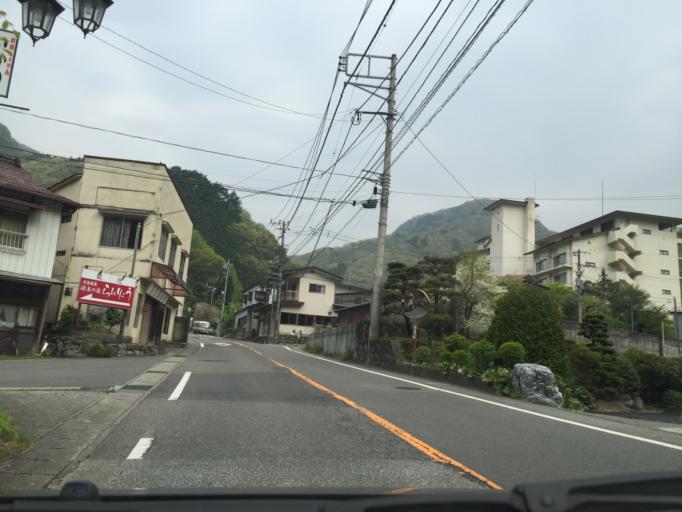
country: JP
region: Tochigi
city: Nikko
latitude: 36.8949
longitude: 139.7110
